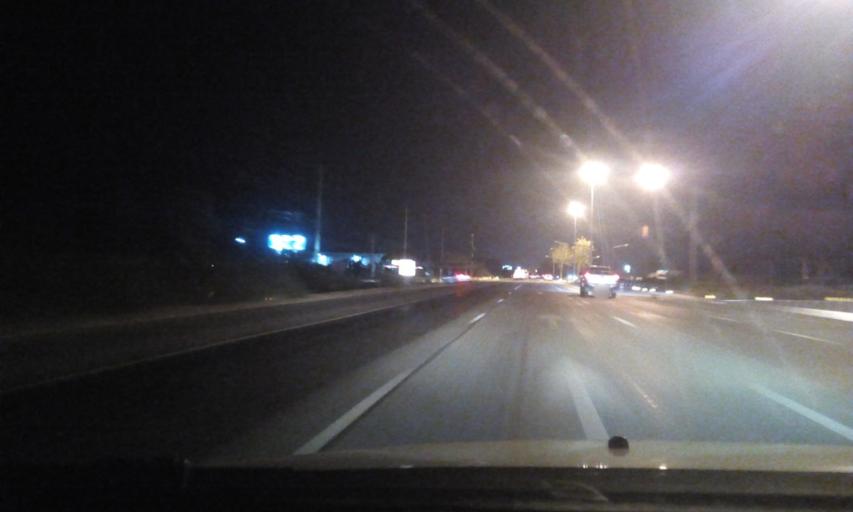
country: TH
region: Sing Buri
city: Phrom Buri
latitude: 14.7502
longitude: 100.4539
